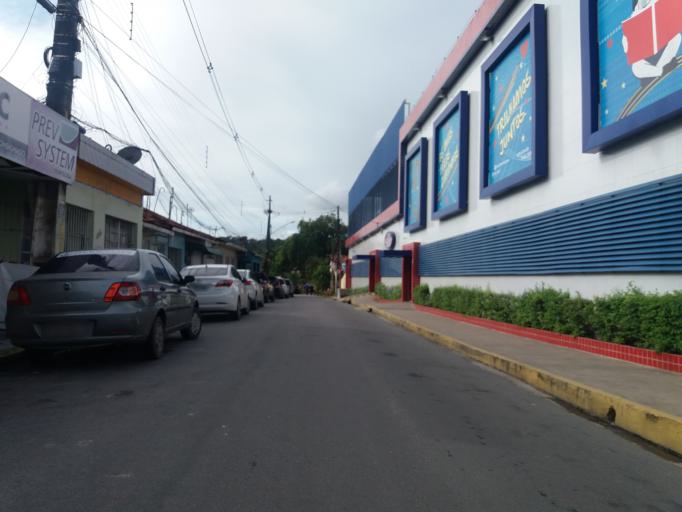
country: BR
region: Pernambuco
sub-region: Paulista
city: Paulista
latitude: -7.9394
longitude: -34.8831
